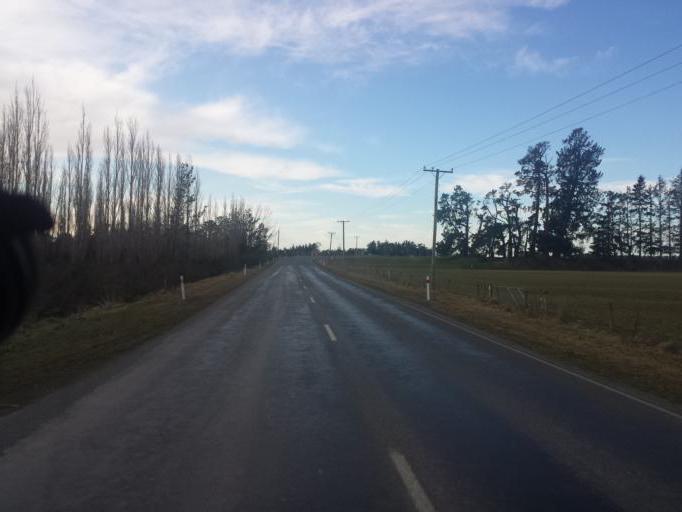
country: NZ
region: Canterbury
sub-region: Ashburton District
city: Methven
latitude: -43.8093
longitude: 171.4311
